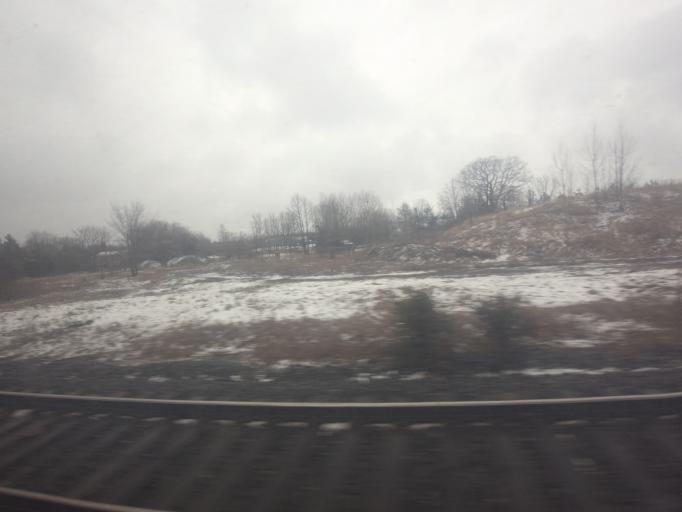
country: CA
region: Ontario
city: Belleville
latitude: 44.2037
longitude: -77.2384
